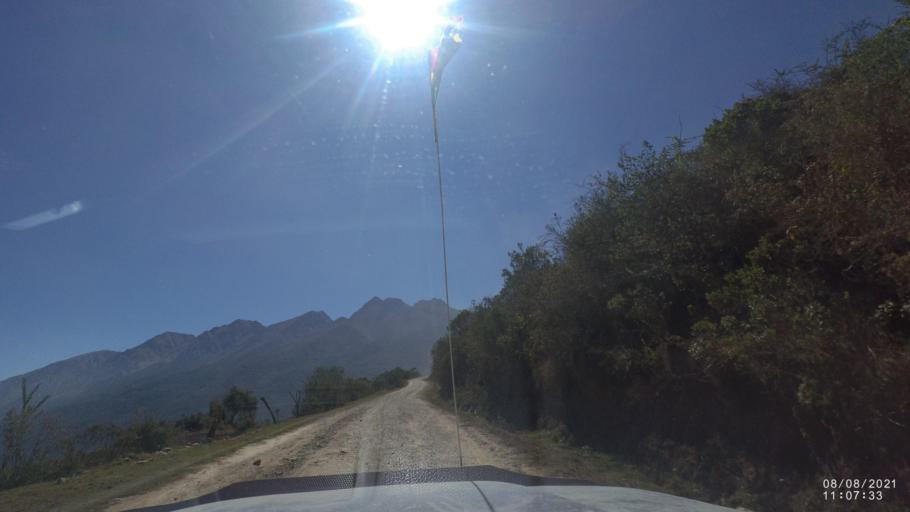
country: BO
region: Cochabamba
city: Colchani
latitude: -16.7632
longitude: -66.6824
